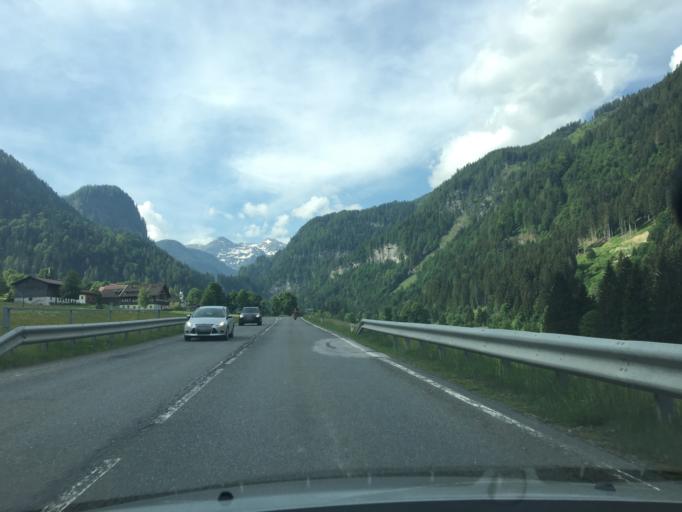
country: AT
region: Salzburg
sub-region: Politischer Bezirk Sankt Johann im Pongau
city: Untertauern
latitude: 47.3093
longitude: 13.5071
